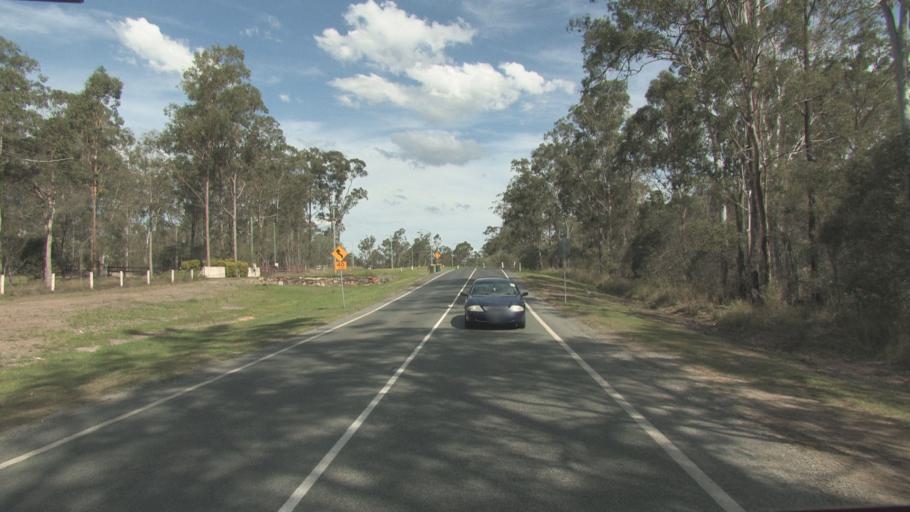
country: AU
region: Queensland
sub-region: Logan
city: Cedar Vale
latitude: -27.8344
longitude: 153.0440
